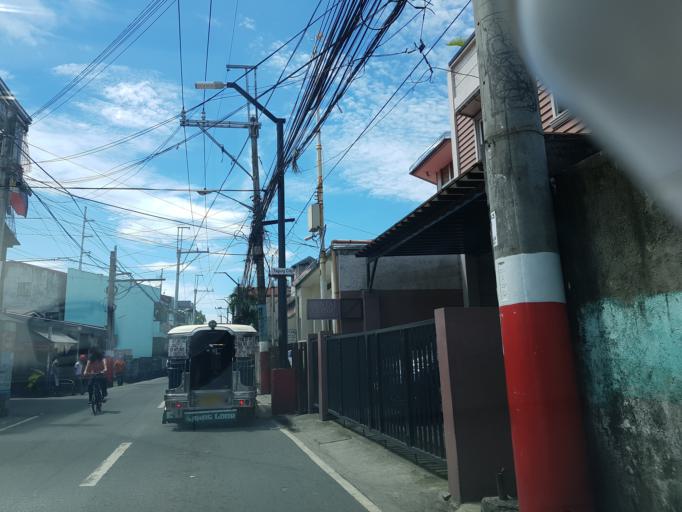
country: PH
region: Calabarzon
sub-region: Province of Rizal
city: Taguig
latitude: 14.5260
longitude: 121.0729
